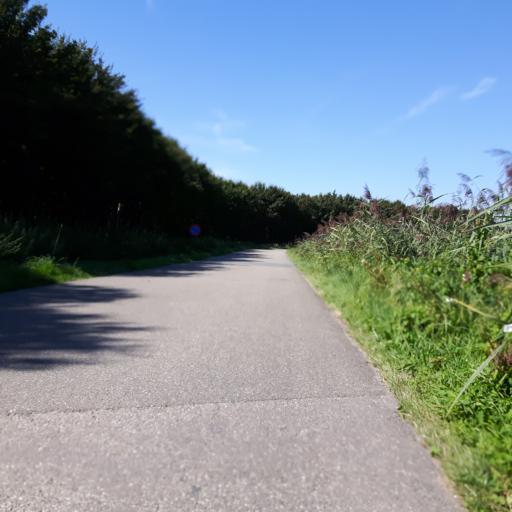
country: NL
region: Zeeland
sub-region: Schouwen-Duiveland
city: Bruinisse
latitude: 51.6203
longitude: 3.9861
